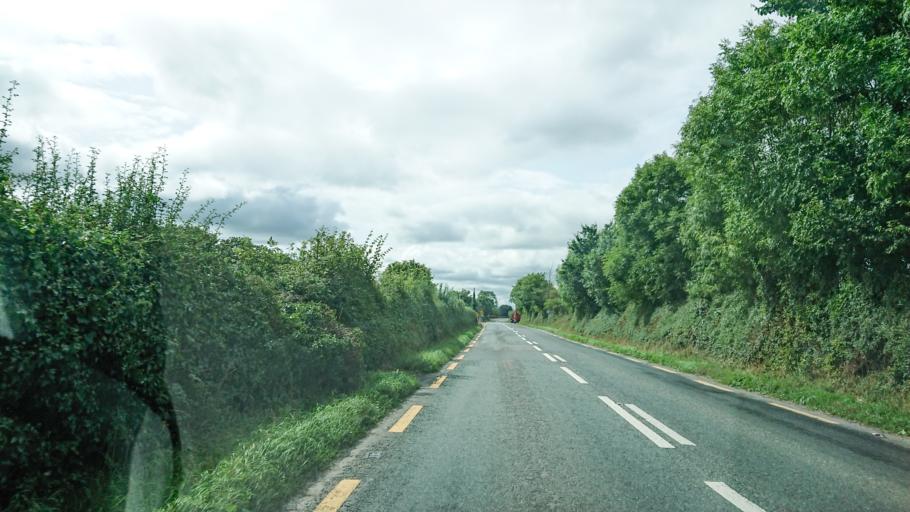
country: IE
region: Munster
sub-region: Waterford
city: Dungarvan
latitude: 52.1217
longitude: -7.7585
